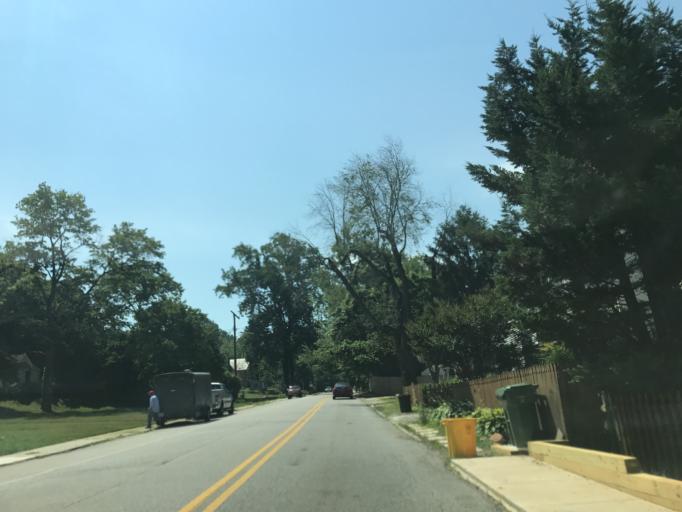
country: US
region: Maryland
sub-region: Baltimore County
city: Pikesville
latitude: 39.3624
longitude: -76.6681
